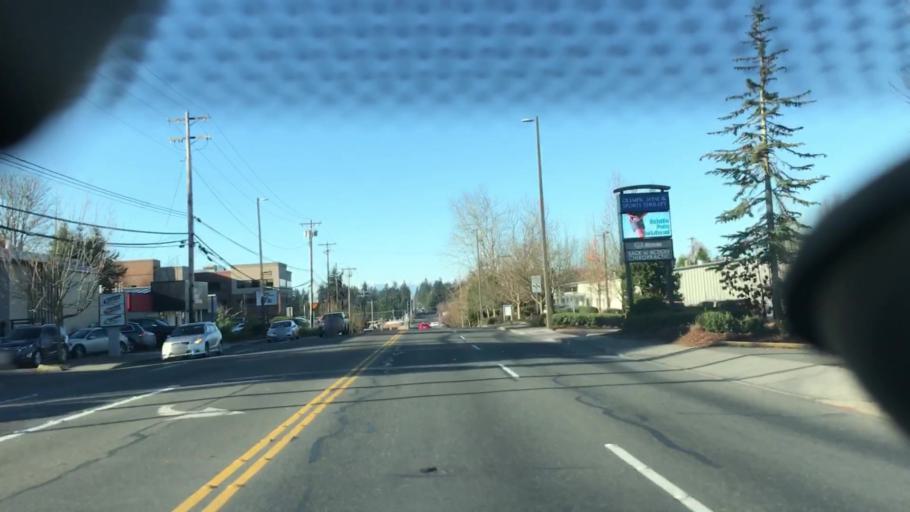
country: US
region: Washington
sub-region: Snohomish County
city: Mountlake Terrace
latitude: 47.7996
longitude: -122.3226
